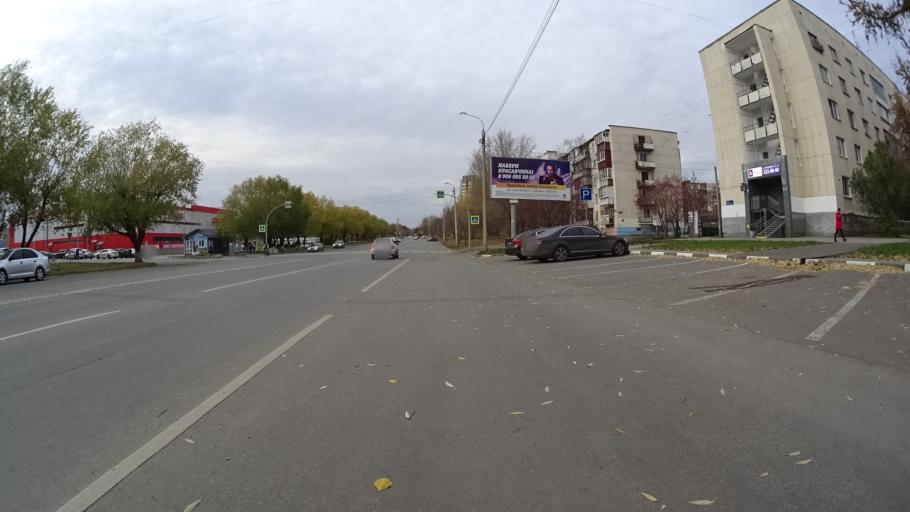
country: RU
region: Chelyabinsk
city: Roshchino
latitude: 55.1916
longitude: 61.3046
